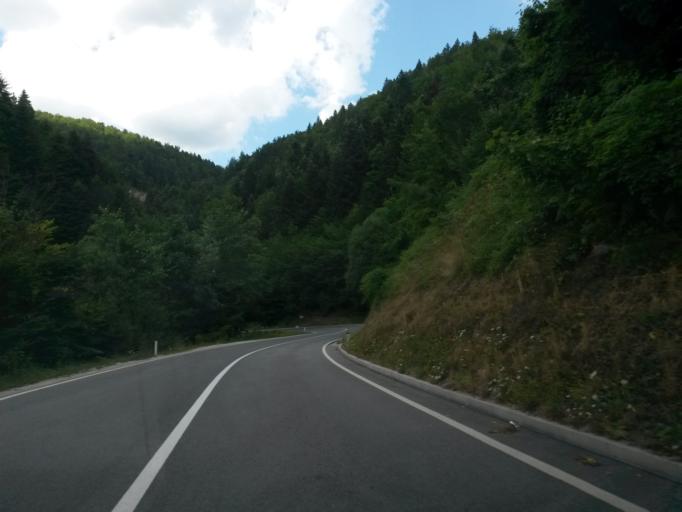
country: BA
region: Federation of Bosnia and Herzegovina
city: Bugojno
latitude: 44.0282
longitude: 17.3536
